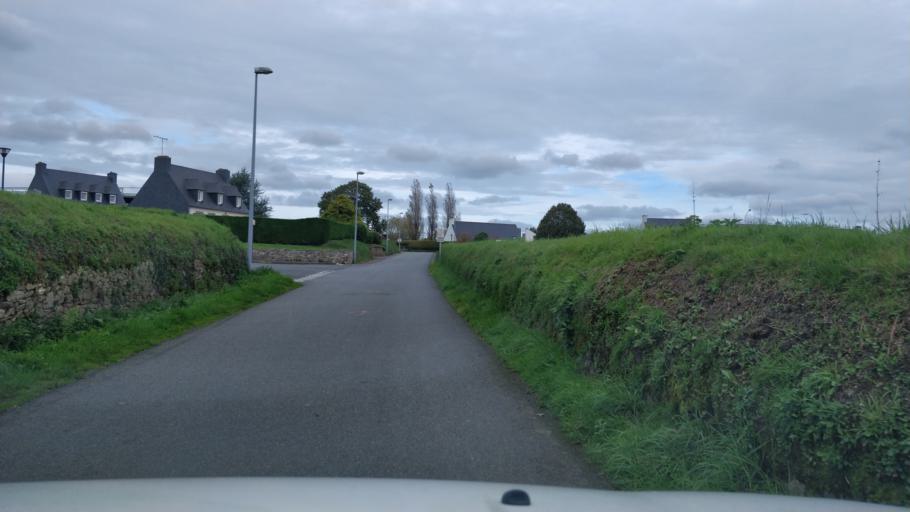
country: FR
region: Brittany
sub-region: Departement des Cotes-d'Armor
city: Minihy-Treguier
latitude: 48.7759
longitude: -3.2308
